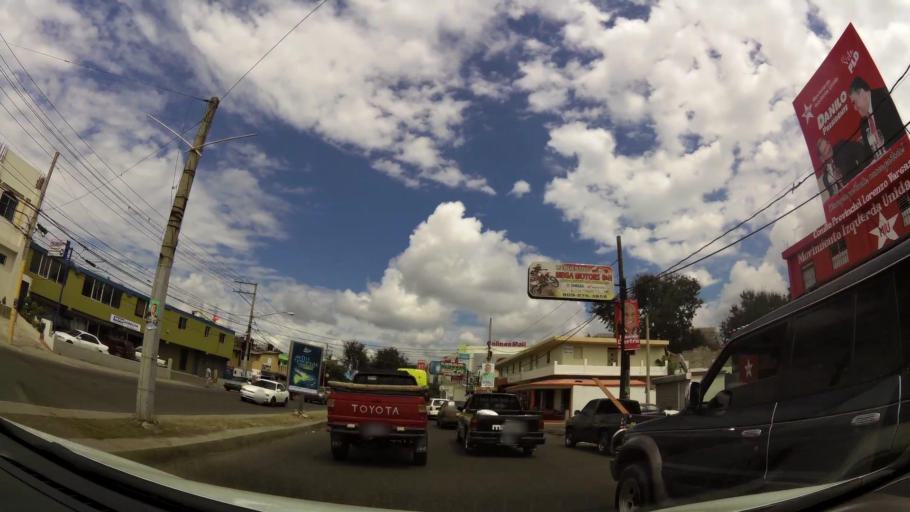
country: DO
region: Santiago
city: Santiago de los Caballeros
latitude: 19.4710
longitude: -70.7134
